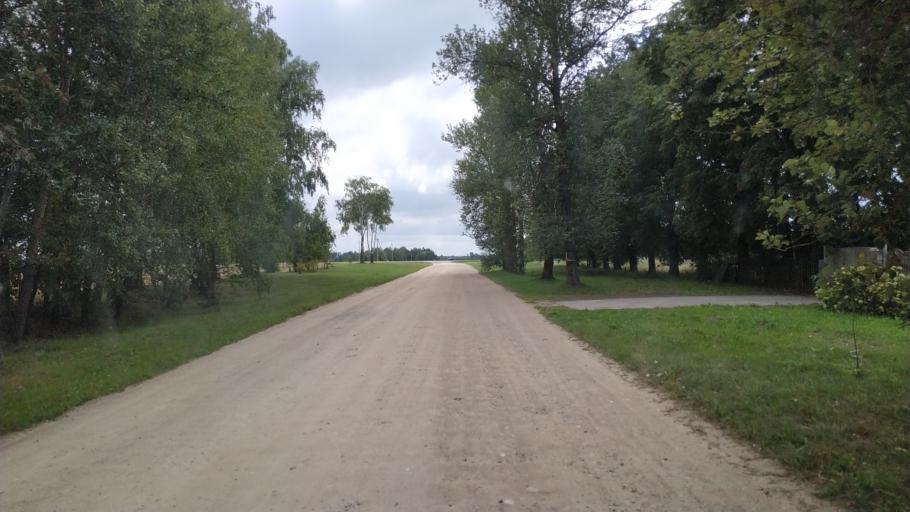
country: BY
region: Mogilev
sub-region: Mahilyowski Rayon
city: Kadino
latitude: 53.8461
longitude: 30.4760
